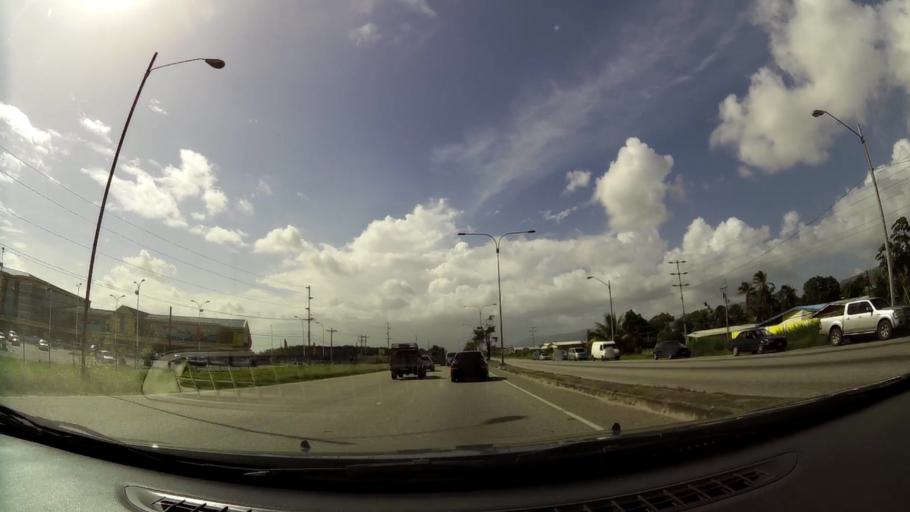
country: TT
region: Borough of Arima
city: Arima
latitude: 10.6100
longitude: -61.2921
